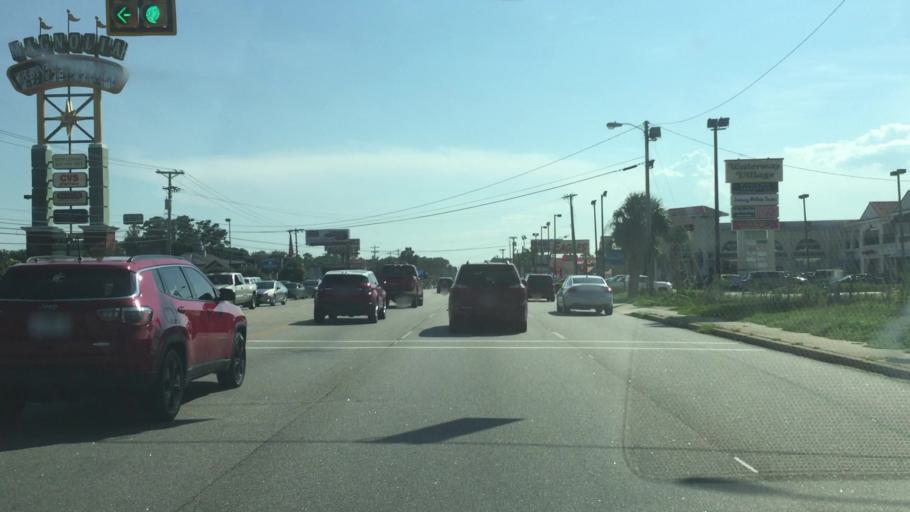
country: US
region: South Carolina
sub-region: Horry County
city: North Myrtle Beach
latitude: 33.7810
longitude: -78.7896
